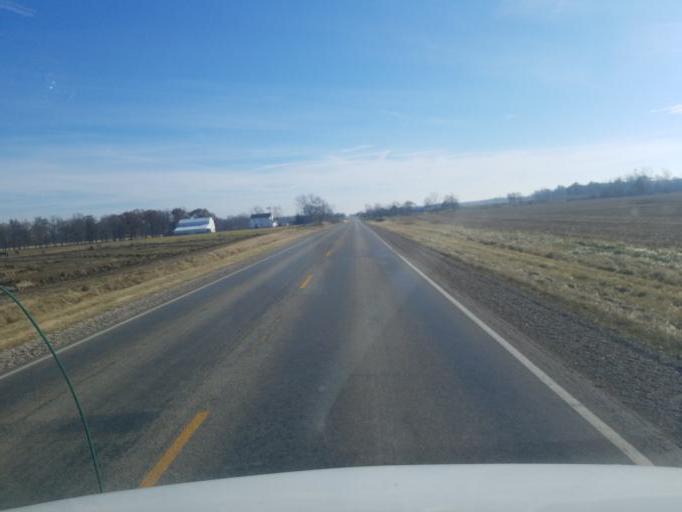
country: US
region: Indiana
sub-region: Adams County
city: Geneva
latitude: 40.5415
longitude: -84.9478
